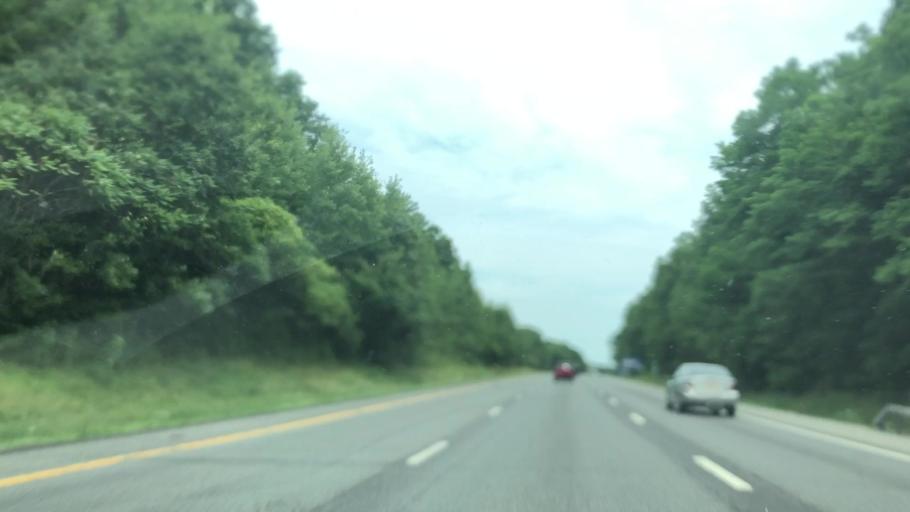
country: US
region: New York
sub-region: Saratoga County
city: Ballston Spa
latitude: 43.0067
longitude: -73.8013
